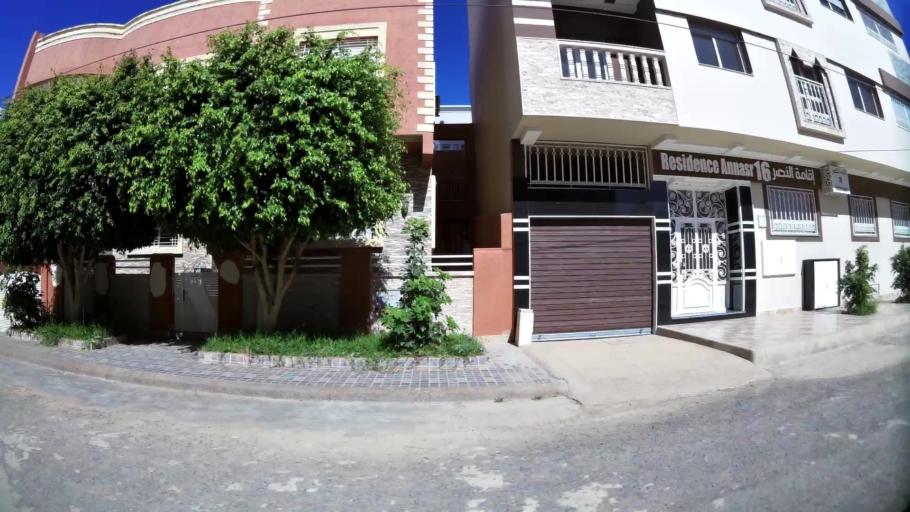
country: MA
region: Oriental
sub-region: Berkane-Taourirt
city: Berkane
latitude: 34.9415
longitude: -2.3295
